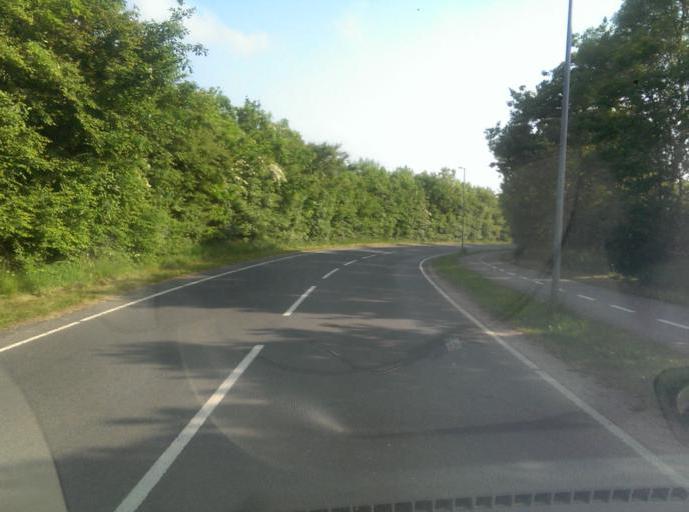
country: DK
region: South Denmark
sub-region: Esbjerg Kommune
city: Bramming
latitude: 55.4248
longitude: 8.6517
